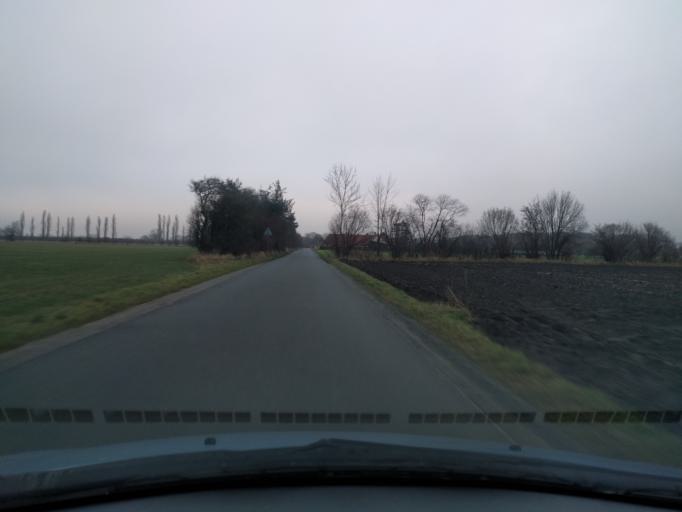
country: DK
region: South Denmark
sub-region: Odense Kommune
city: Bullerup
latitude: 55.4150
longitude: 10.5195
